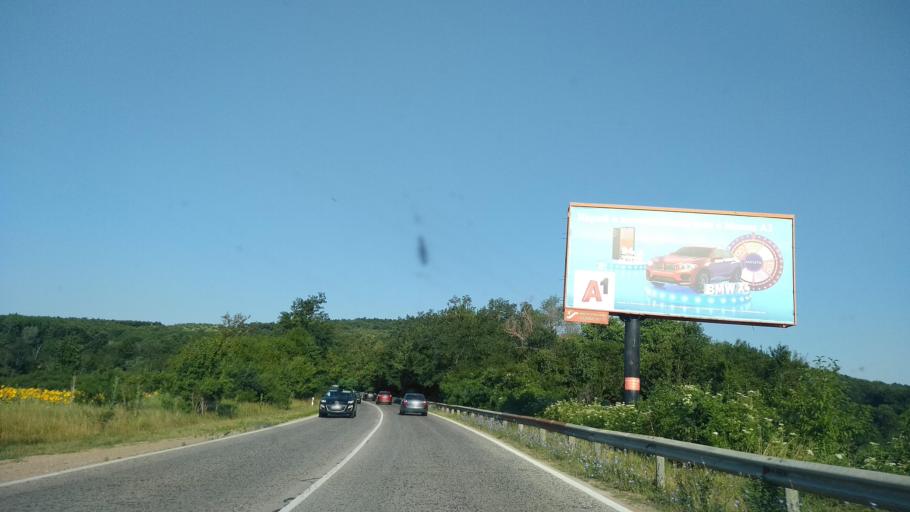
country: BG
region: Lovech
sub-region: Obshtina Lovech
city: Lovech
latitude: 43.0486
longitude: 24.8628
